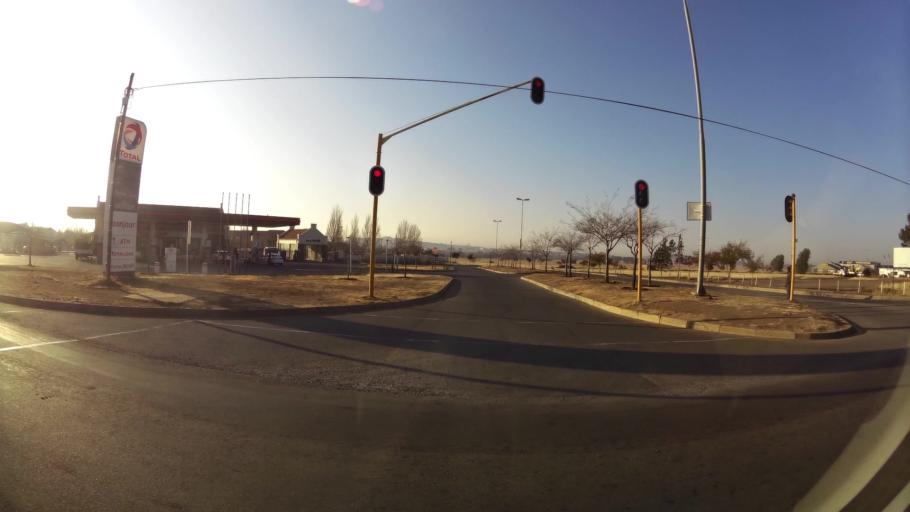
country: ZA
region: Orange Free State
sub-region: Mangaung Metropolitan Municipality
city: Bloemfontein
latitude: -29.1699
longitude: 26.1786
